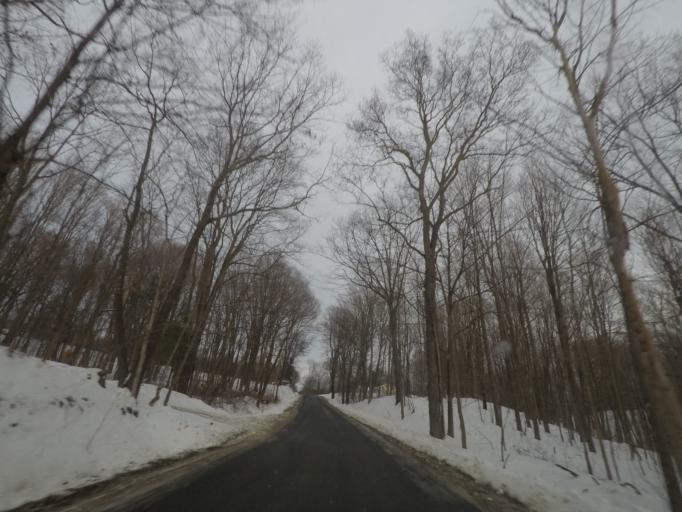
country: US
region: New York
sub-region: Rensselaer County
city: Nassau
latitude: 42.5743
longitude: -73.5882
